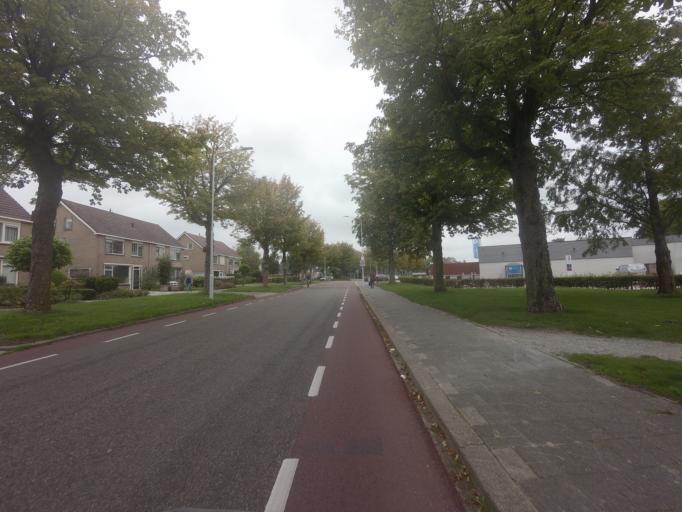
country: NL
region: Friesland
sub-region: Gemeente Leeuwarderadeel
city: Stiens
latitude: 53.2573
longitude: 5.7641
